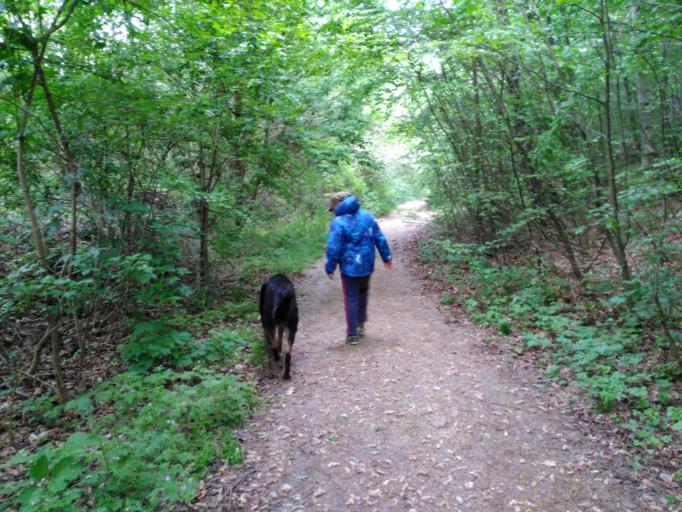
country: CZ
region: Central Bohemia
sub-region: Okres Beroun
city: Kraluv Dvur
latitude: 49.9181
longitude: 14.0548
